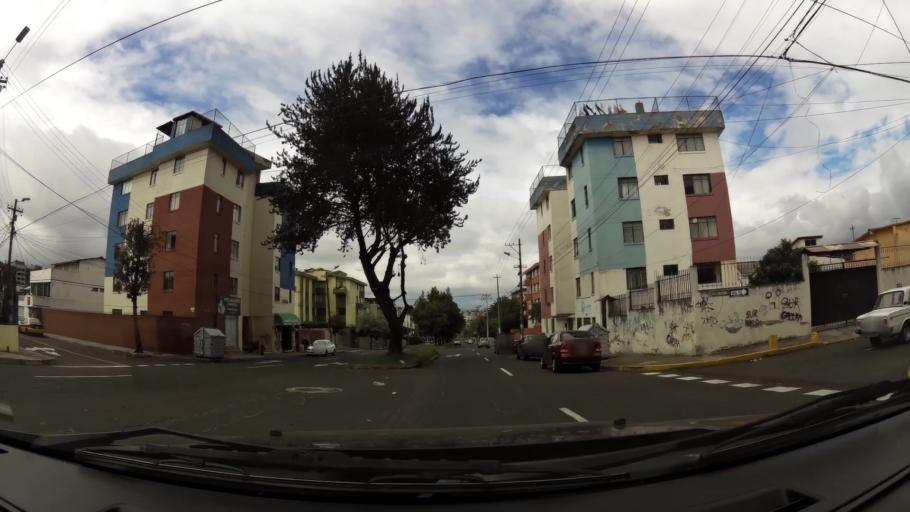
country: EC
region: Pichincha
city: Quito
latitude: -0.1372
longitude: -78.4994
